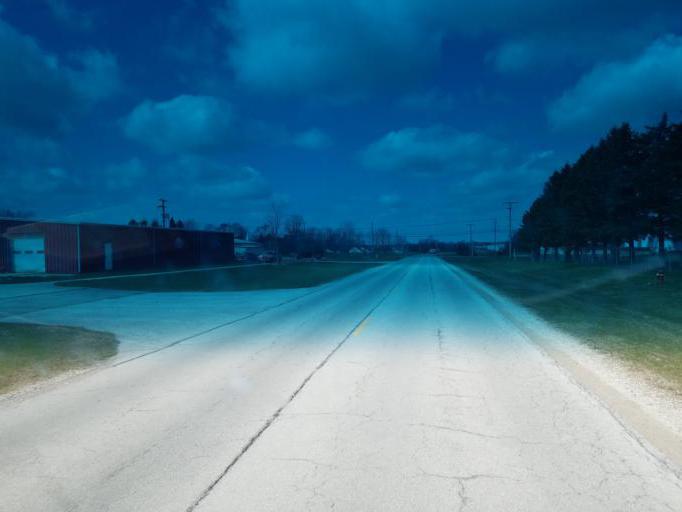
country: US
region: Ohio
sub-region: Crawford County
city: Bucyrus
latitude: 40.7897
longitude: -82.9567
